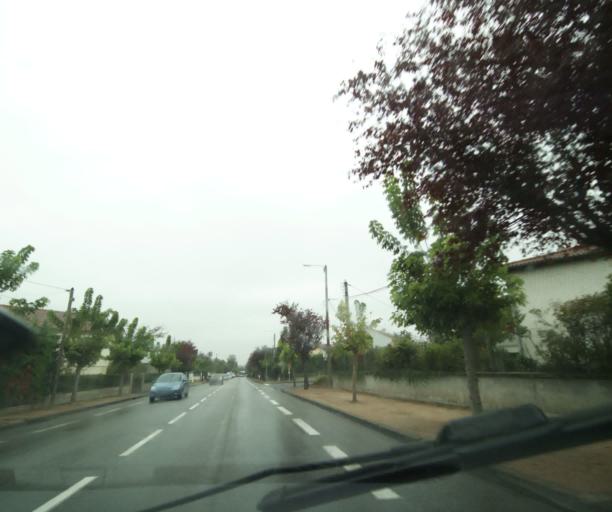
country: FR
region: Auvergne
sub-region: Departement du Puy-de-Dome
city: Cebazat
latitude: 45.8240
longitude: 3.1057
